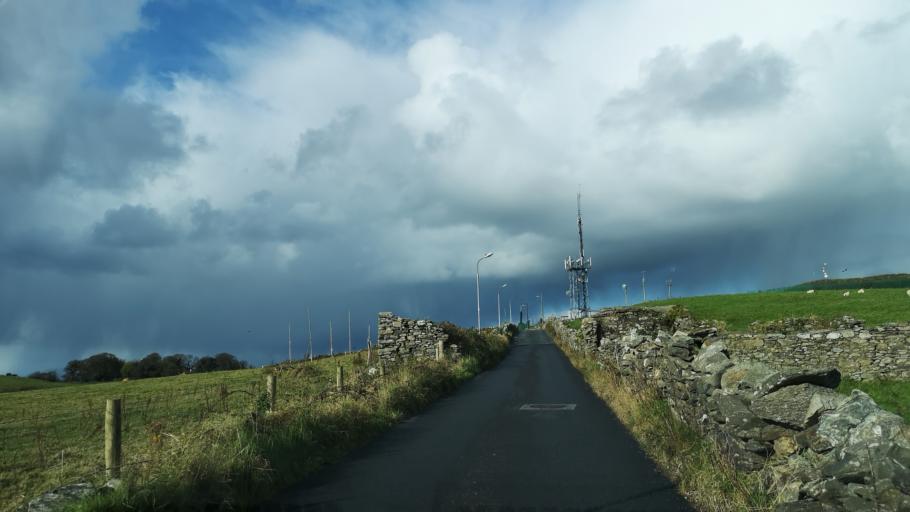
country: IE
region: Connaught
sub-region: Maigh Eo
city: Westport
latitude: 53.7946
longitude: -9.5171
